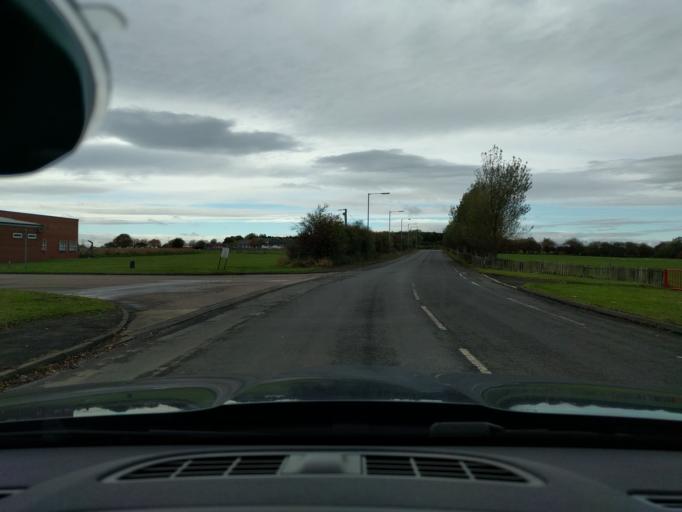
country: GB
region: England
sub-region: Northumberland
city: Ashington
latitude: 55.1562
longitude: -1.5457
